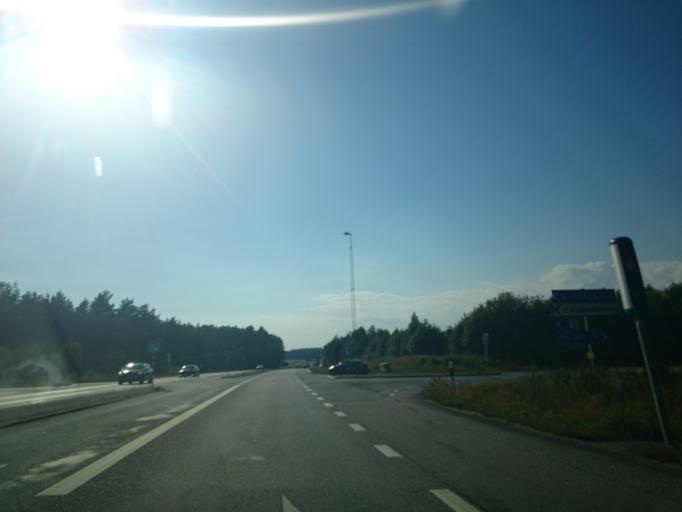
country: SE
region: Blekinge
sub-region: Ronneby Kommun
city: Kallinge
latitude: 56.1997
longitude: 15.3760
